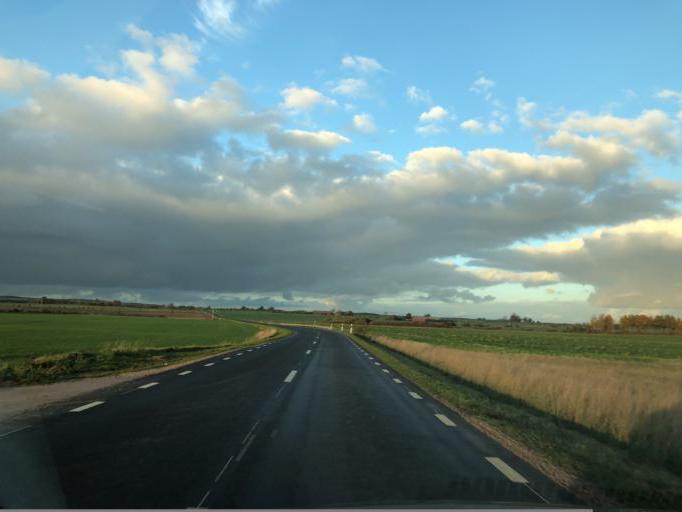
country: SE
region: Skane
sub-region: Svalovs Kommun
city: Svaloev
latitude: 55.9064
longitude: 13.1965
